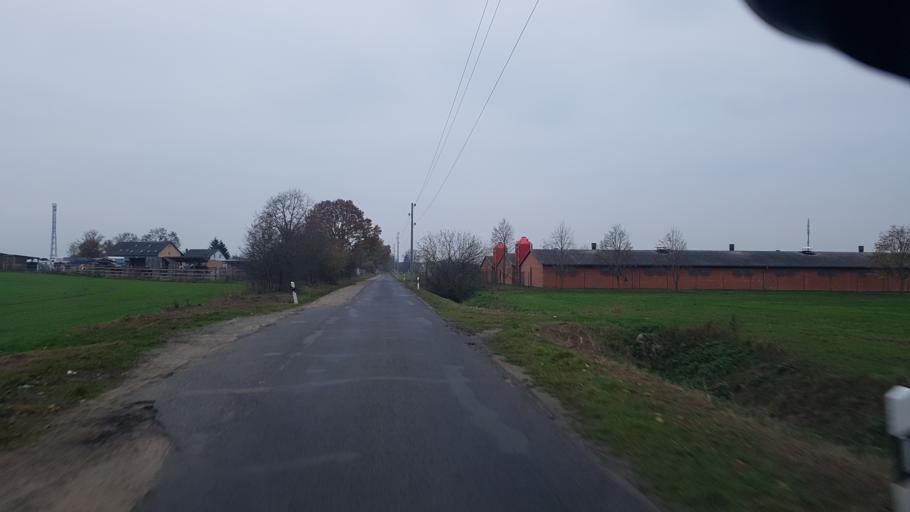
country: DE
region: Brandenburg
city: Ruthnick
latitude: 52.9096
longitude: 12.9812
